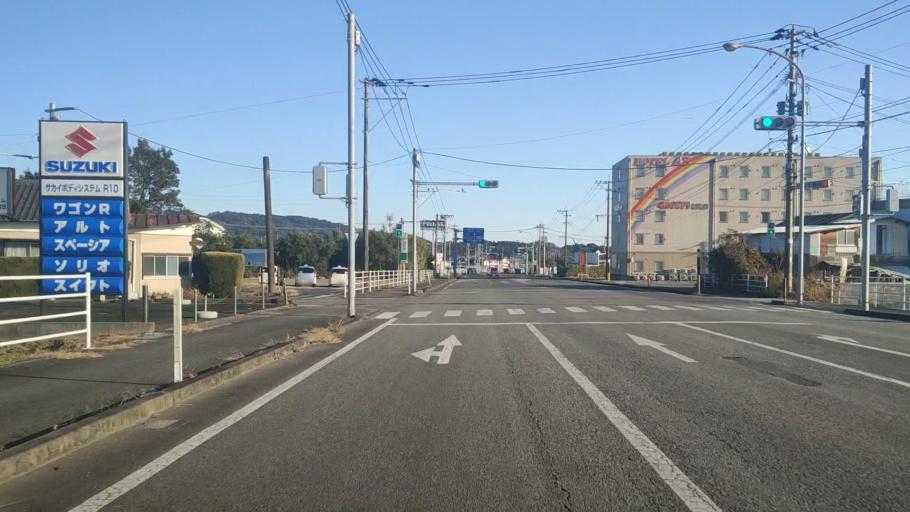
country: JP
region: Miyazaki
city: Takanabe
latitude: 32.2527
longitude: 131.5529
